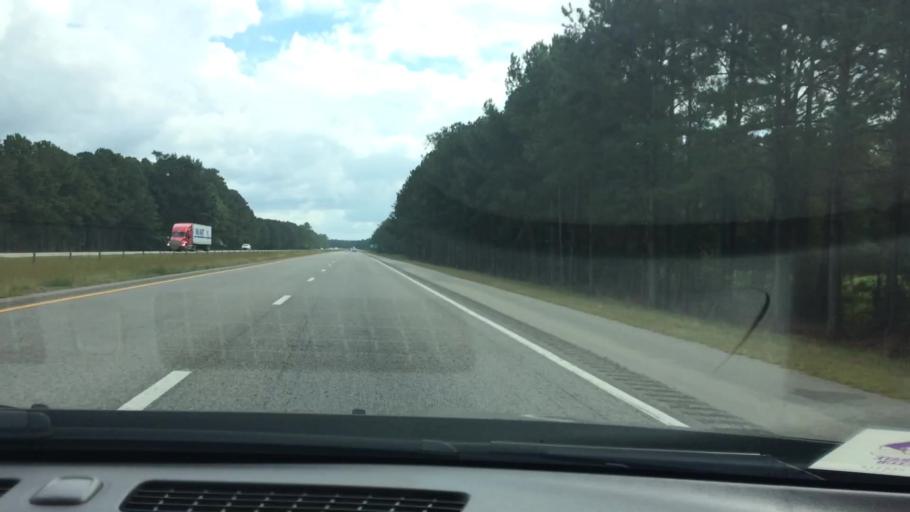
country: US
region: North Carolina
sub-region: Pitt County
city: Farmville
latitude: 35.6381
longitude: -77.7260
